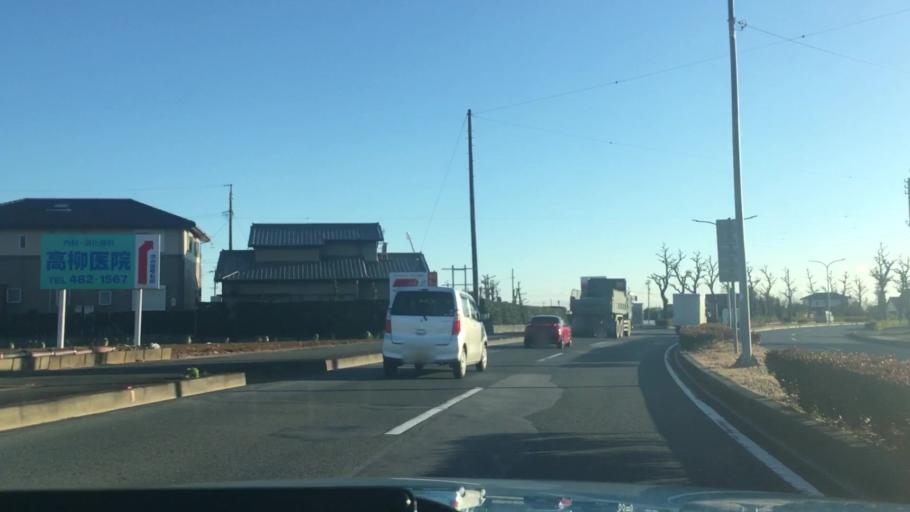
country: JP
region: Shizuoka
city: Hamamatsu
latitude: 34.7416
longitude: 137.6672
